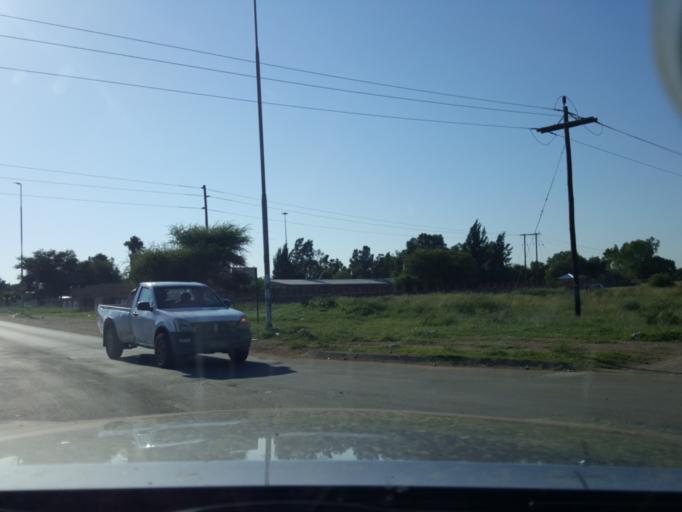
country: ZA
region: North-West
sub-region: Ngaka Modiri Molema District Municipality
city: Mmabatho
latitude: -25.8257
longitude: 25.6357
